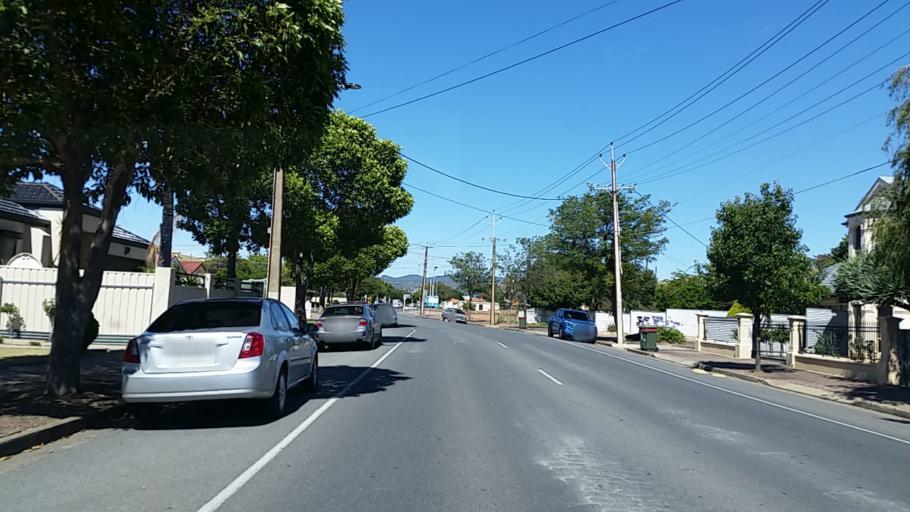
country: AU
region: South Australia
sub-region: Marion
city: South Plympton
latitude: -34.9803
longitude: 138.5619
